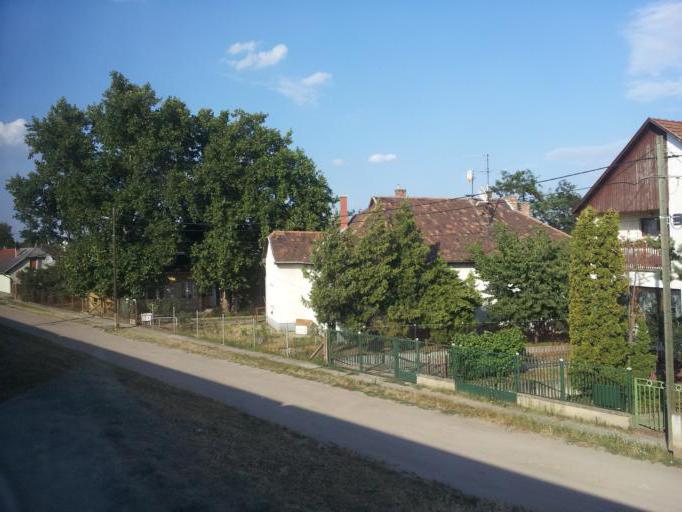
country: HU
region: Pest
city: Dunaharaszti
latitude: 47.3543
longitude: 19.0981
